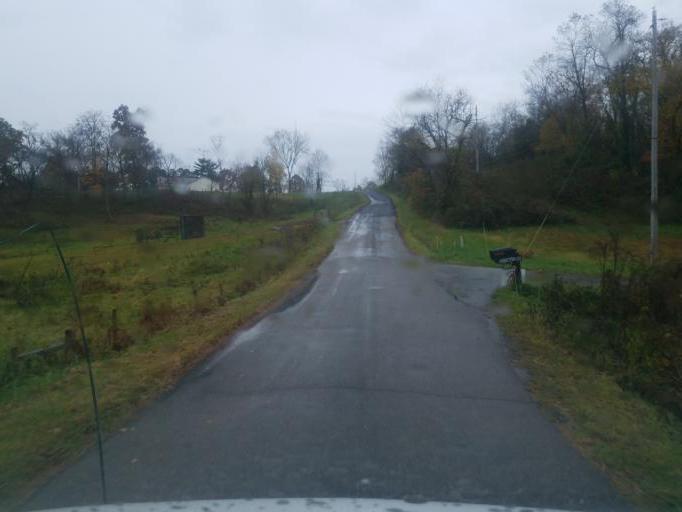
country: US
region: West Virginia
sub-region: Wood County
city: Blennerhassett
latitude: 39.3234
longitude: -81.6152
